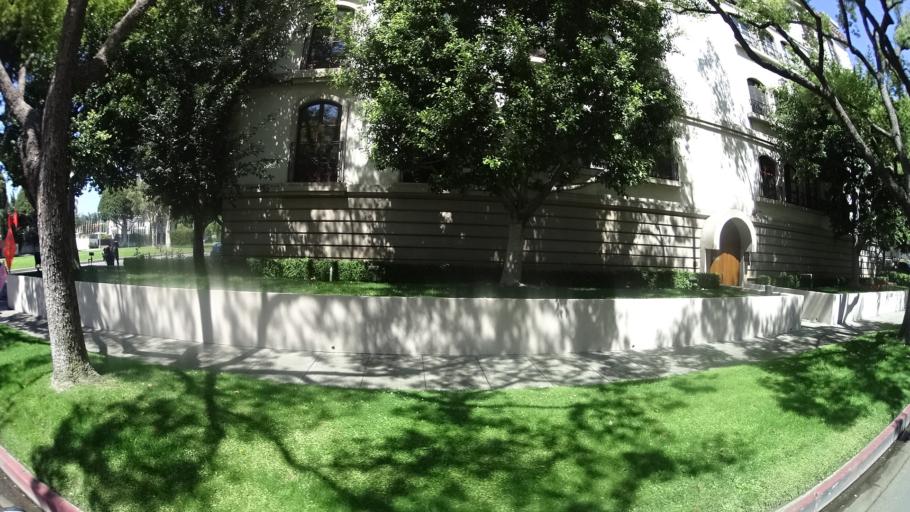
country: US
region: California
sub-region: Los Angeles County
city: Beverly Hills
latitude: 34.0726
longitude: -118.3936
